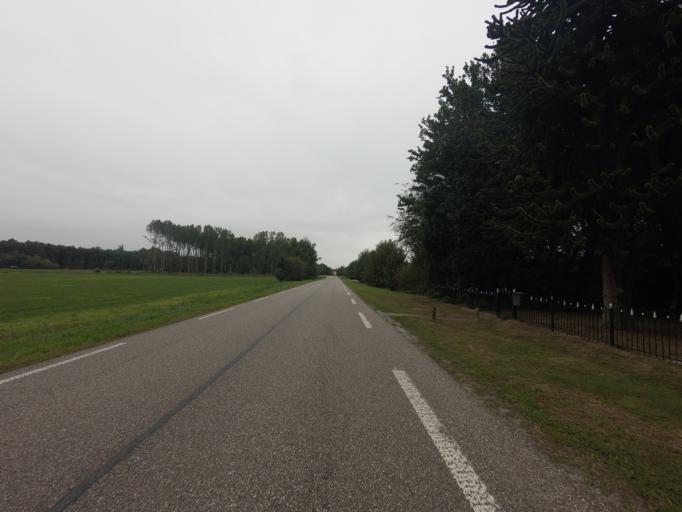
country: NL
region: Friesland
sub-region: Gemeente Opsterland
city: Tijnje
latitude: 53.0254
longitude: 6.0003
